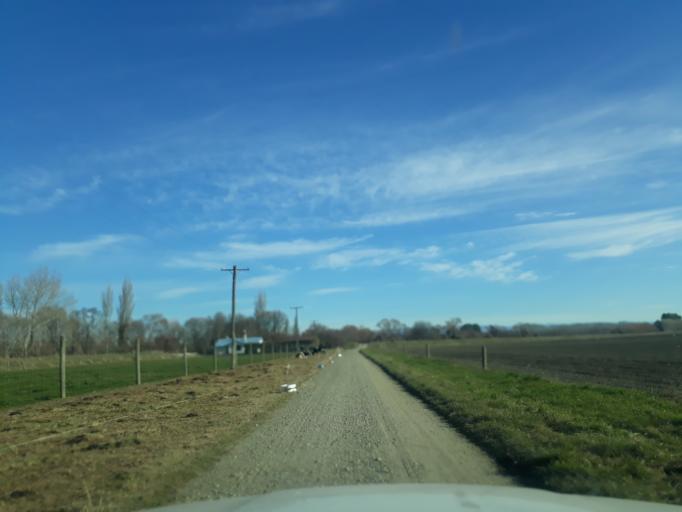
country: NZ
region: Canterbury
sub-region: Timaru District
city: Timaru
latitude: -44.2692
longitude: 171.3348
